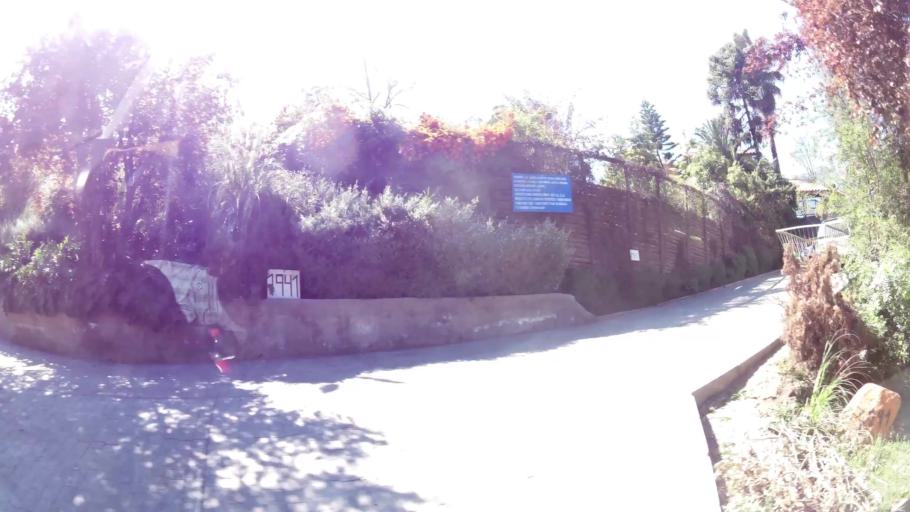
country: CL
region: Santiago Metropolitan
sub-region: Provincia de Santiago
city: Villa Presidente Frei, Nunoa, Santiago, Chile
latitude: -33.4391
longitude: -70.5190
